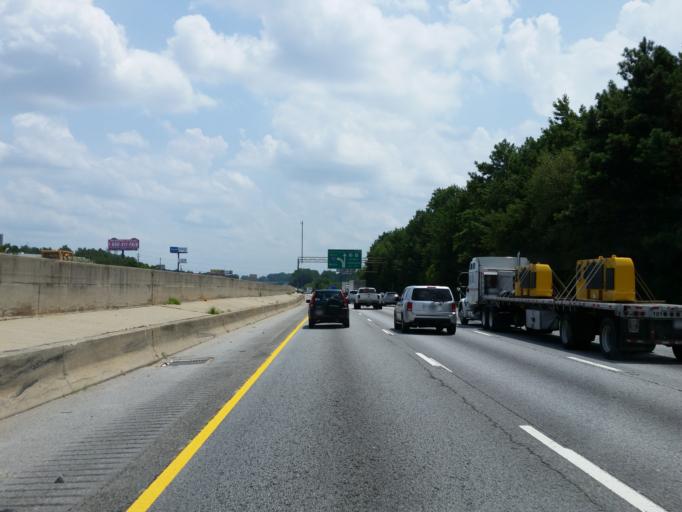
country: US
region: Georgia
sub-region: Clayton County
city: Forest Park
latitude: 33.6016
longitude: -84.3922
